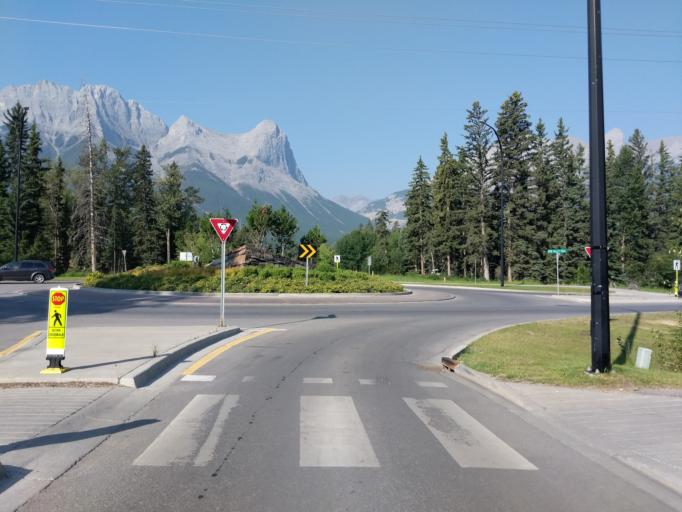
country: CA
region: Alberta
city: Canmore
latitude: 51.0849
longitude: -115.3441
